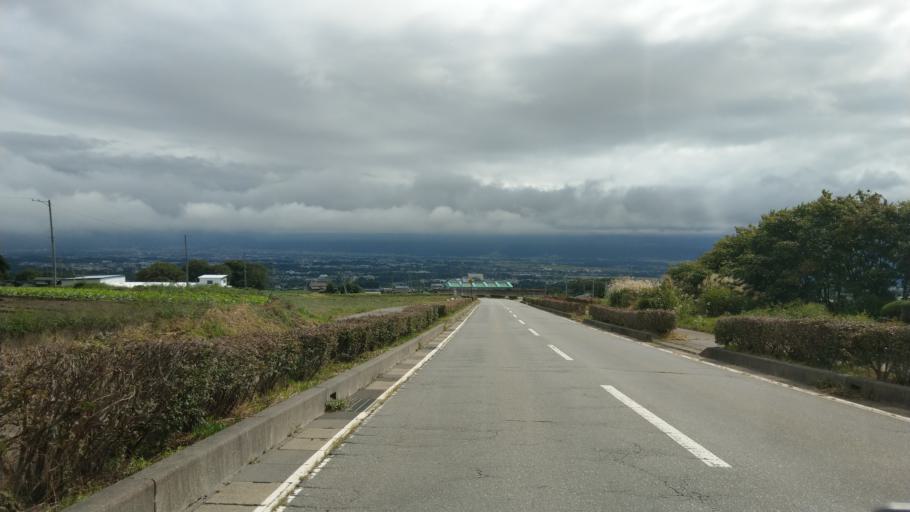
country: JP
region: Nagano
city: Komoro
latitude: 36.3376
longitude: 138.4585
